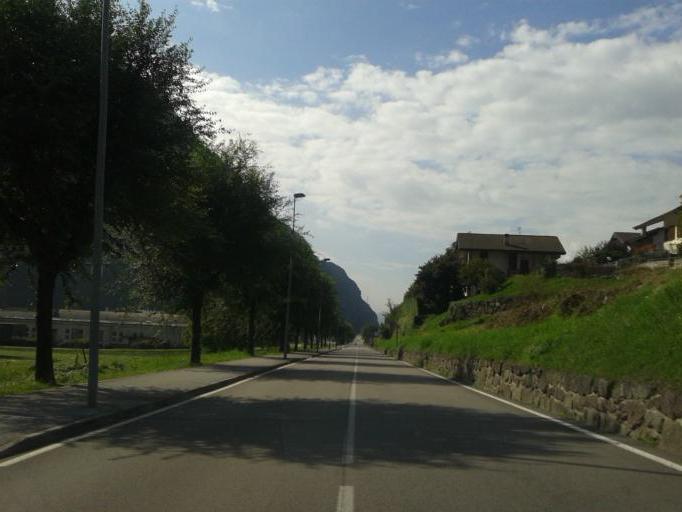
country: IT
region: Trentino-Alto Adige
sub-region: Provincia di Trento
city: Condino
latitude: 45.8843
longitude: 10.5955
